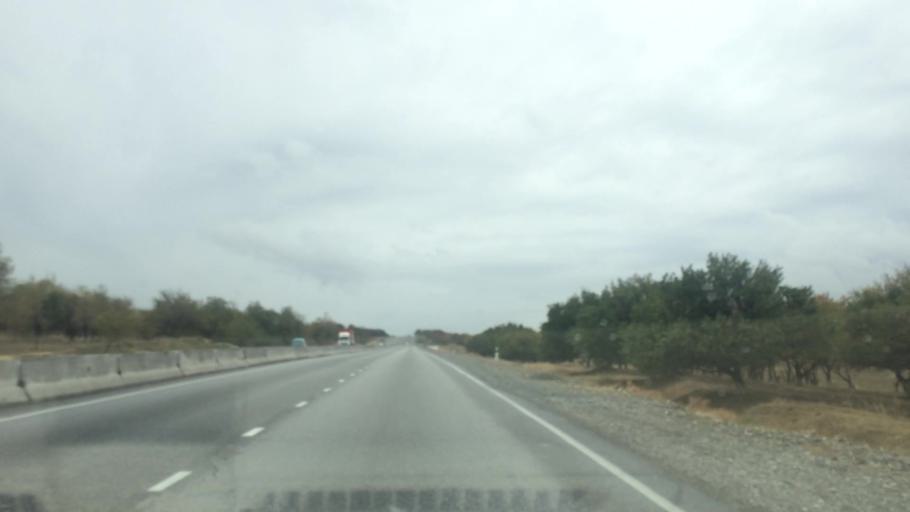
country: UZ
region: Samarqand
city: Bulung'ur
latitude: 39.8656
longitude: 67.4740
